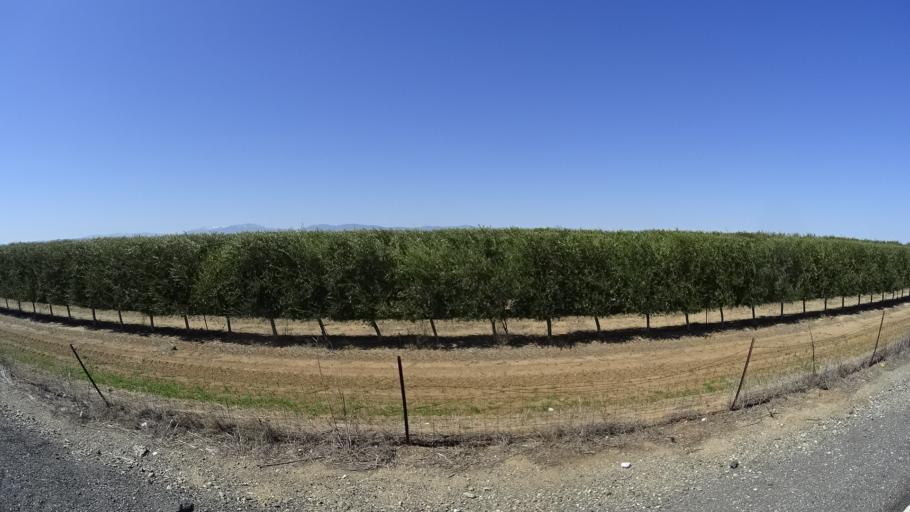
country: US
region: California
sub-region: Glenn County
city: Willows
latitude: 39.5921
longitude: -122.2498
